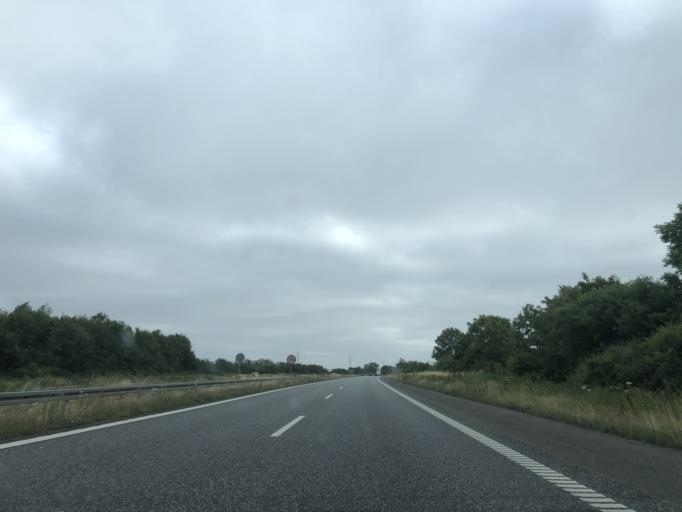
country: DK
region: Central Jutland
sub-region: Arhus Kommune
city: Kolt
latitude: 56.1216
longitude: 10.0904
